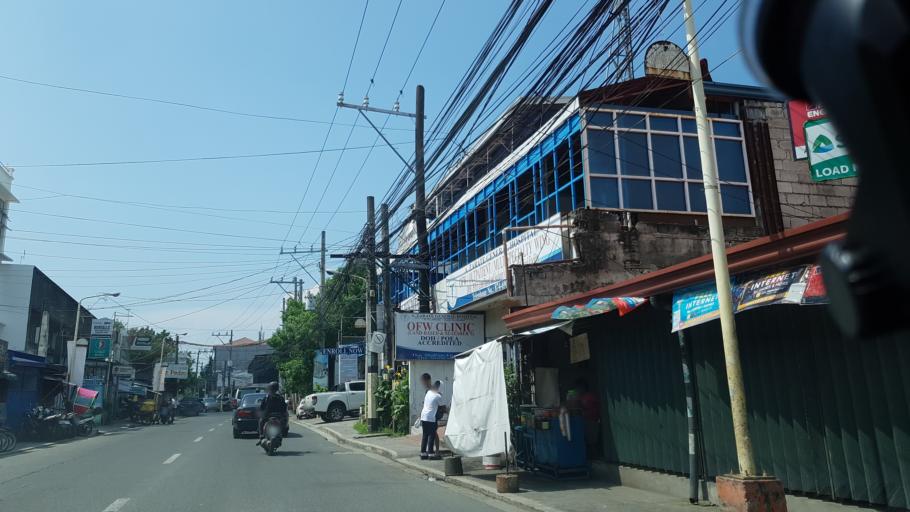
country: PH
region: Calabarzon
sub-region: Province of Rizal
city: Las Pinas
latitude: 14.4684
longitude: 120.9807
